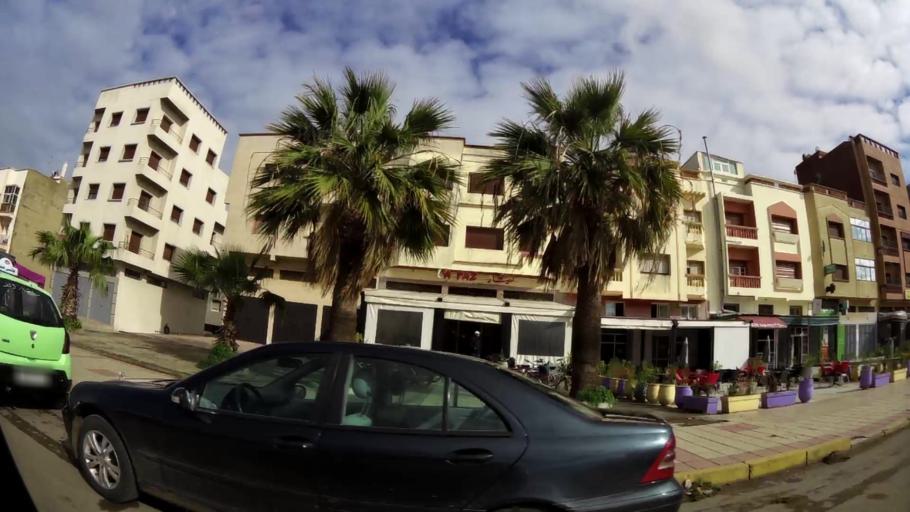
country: MA
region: Grand Casablanca
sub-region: Mohammedia
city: Mohammedia
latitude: 33.6930
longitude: -7.3713
